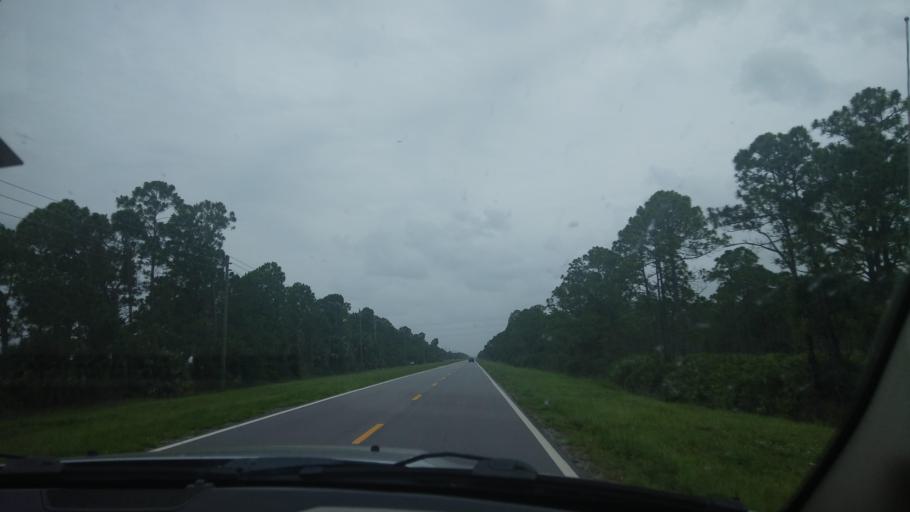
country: US
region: Florida
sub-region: Brevard County
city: Grant-Valkaria
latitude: 27.8626
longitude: -80.6229
